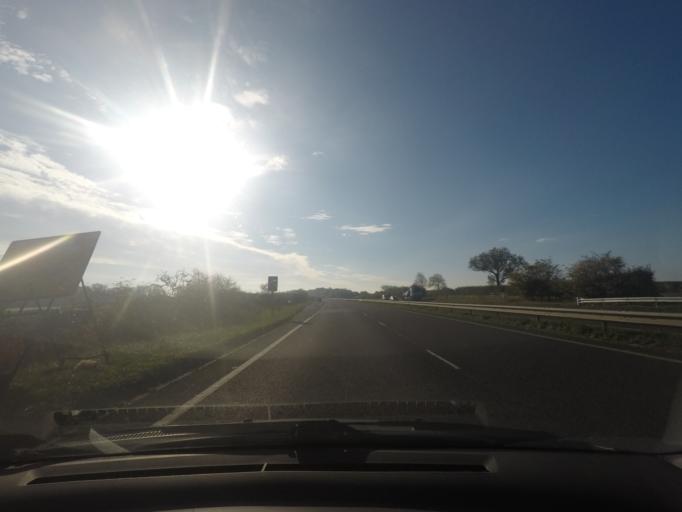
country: GB
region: England
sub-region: North Lincolnshire
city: Barton upon Humber
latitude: 53.6462
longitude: -0.4513
